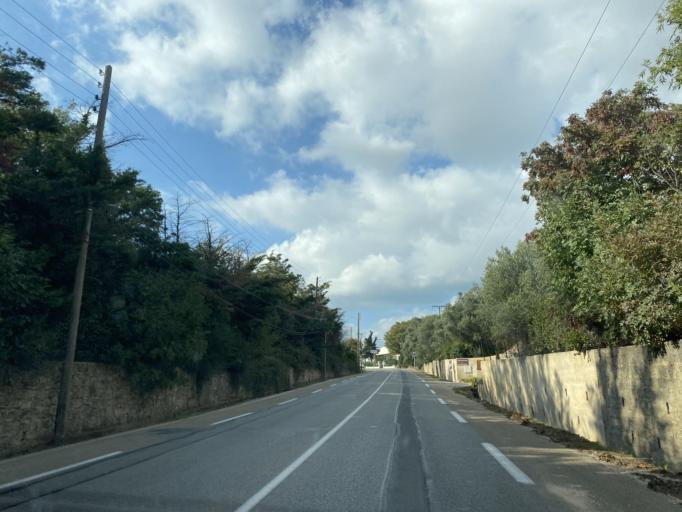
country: FR
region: Provence-Alpes-Cote d'Azur
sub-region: Departement du Var
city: Ollioules
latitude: 43.1272
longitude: 5.8626
